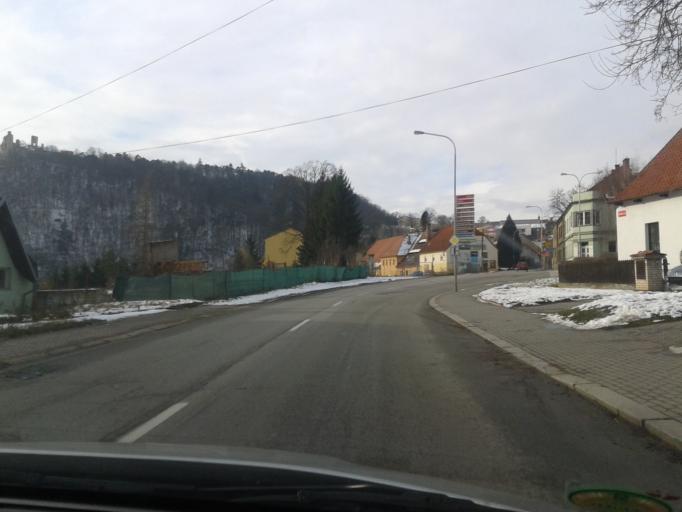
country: CZ
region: South Moravian
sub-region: Okres Blansko
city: Boskovice
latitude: 49.4836
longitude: 16.6703
